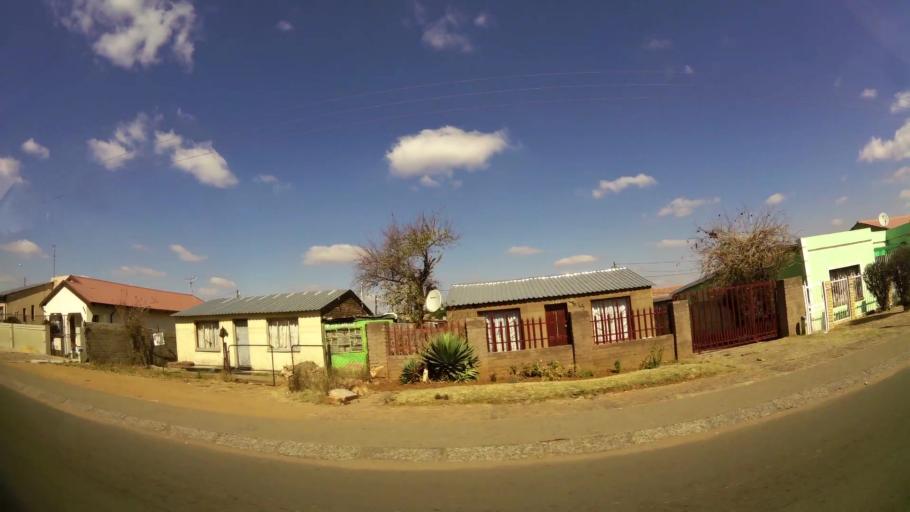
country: ZA
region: Gauteng
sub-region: West Rand District Municipality
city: Krugersdorp
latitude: -26.1537
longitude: 27.7851
